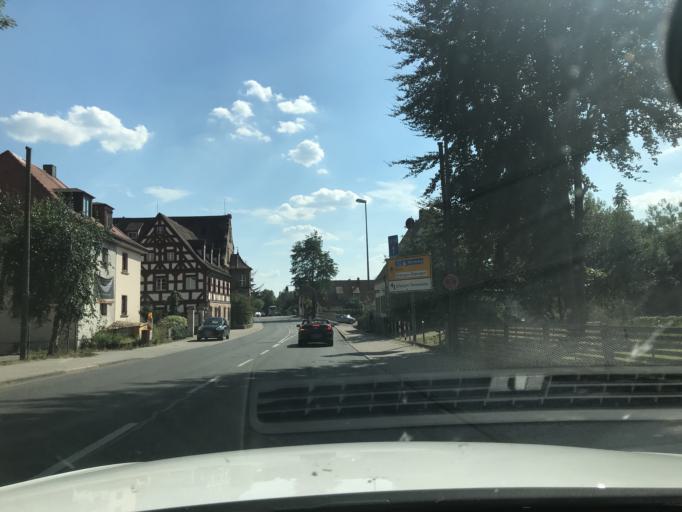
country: DE
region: Bavaria
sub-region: Regierungsbezirk Mittelfranken
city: Erlangen
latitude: 49.5719
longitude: 10.9853
